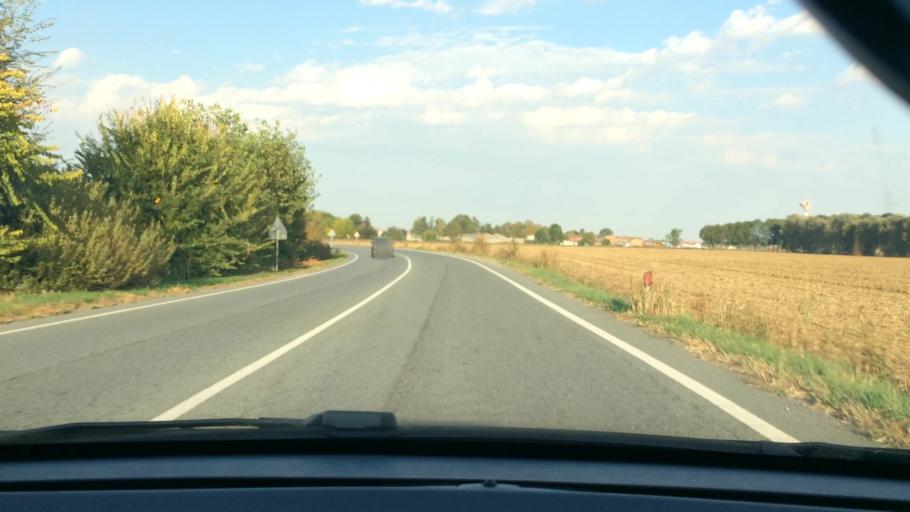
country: IT
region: Piedmont
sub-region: Provincia di Torino
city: Candiolo
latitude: 44.9531
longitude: 7.5891
